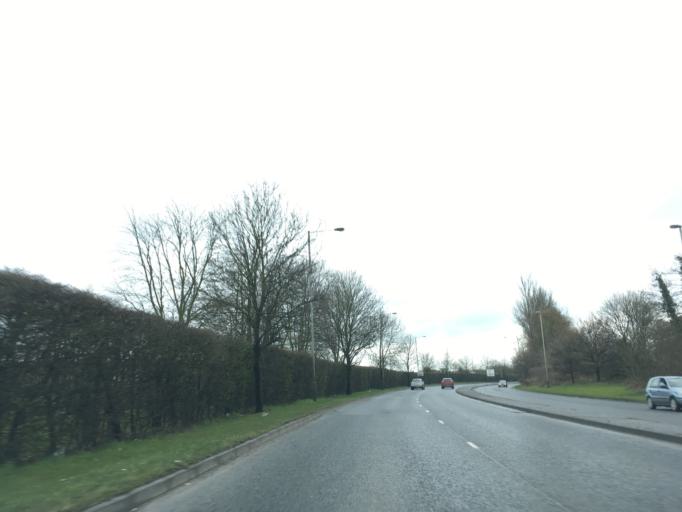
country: GB
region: England
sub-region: Borough of Swindon
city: Swindon
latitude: 51.5698
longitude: -1.7939
